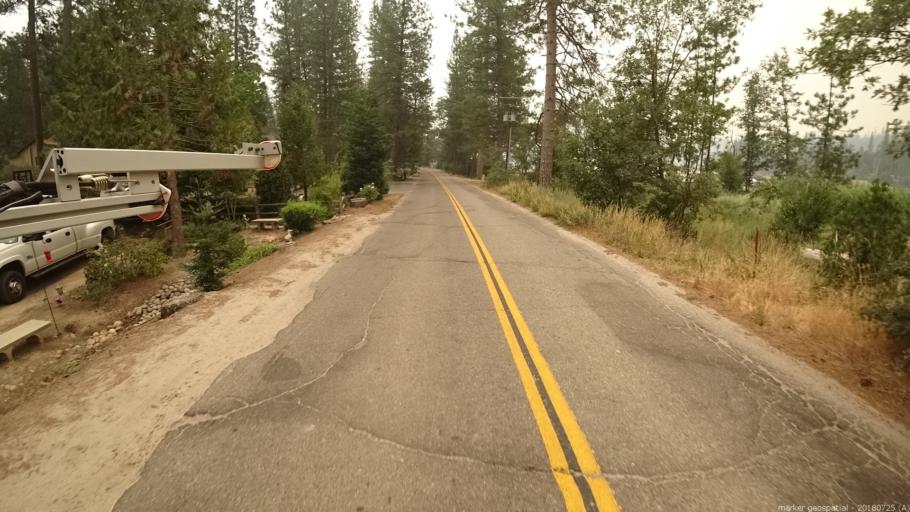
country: US
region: California
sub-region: Madera County
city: Oakhurst
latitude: 37.3321
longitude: -119.5776
